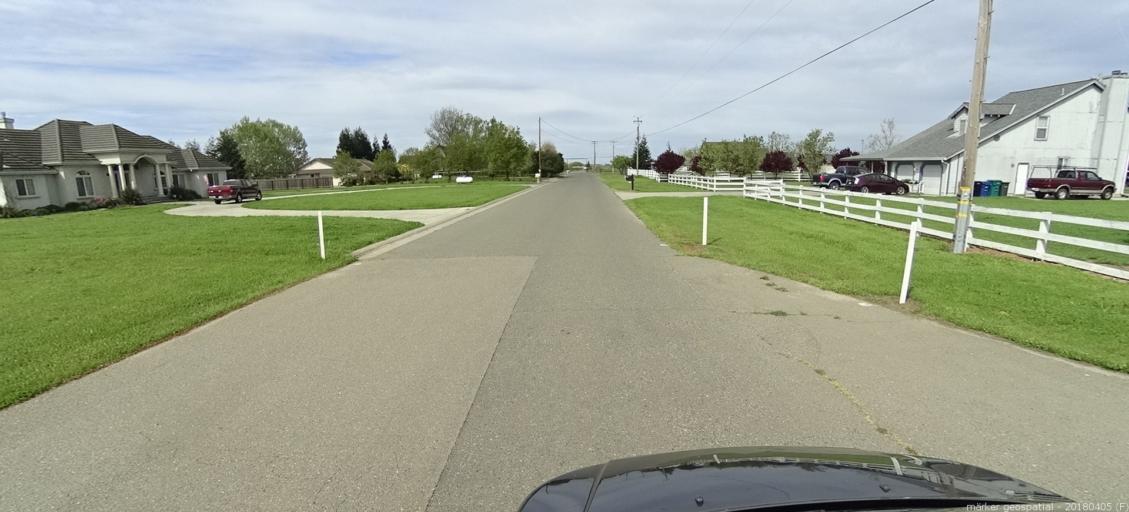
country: US
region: California
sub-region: Sacramento County
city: Galt
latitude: 38.2727
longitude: -121.3349
